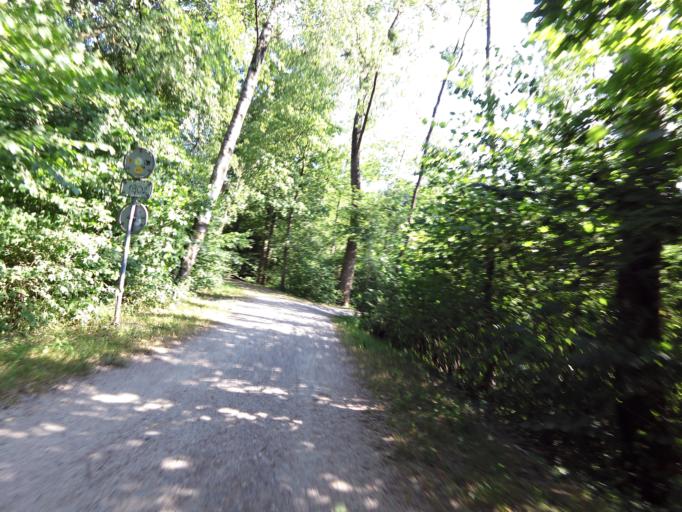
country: CH
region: Aargau
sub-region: Bezirk Lenzburg
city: Niederlenz
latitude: 47.4193
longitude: 8.1633
